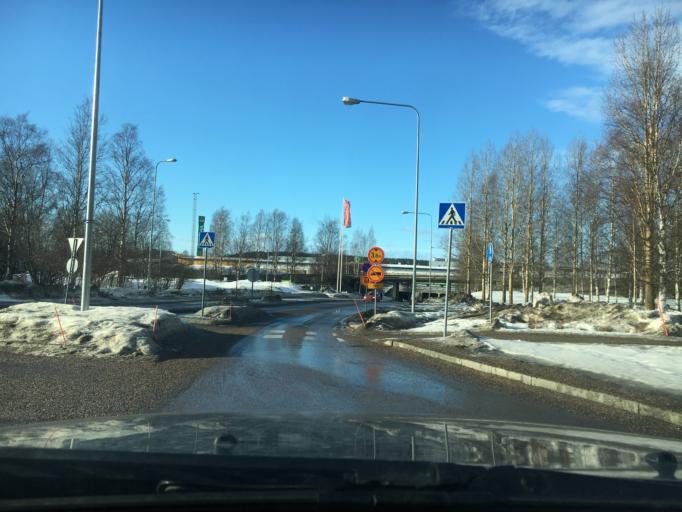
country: FI
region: Kainuu
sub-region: Kajaani
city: Kajaani
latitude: 64.2179
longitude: 27.7459
